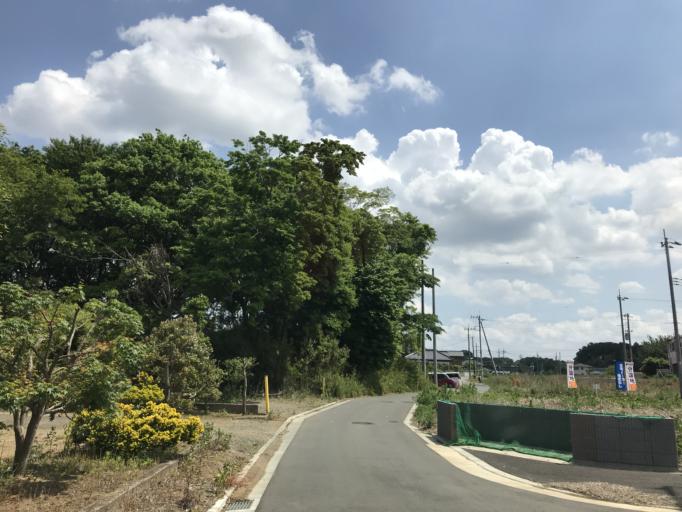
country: JP
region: Ibaraki
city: Mitsukaido
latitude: 36.0706
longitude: 140.0430
